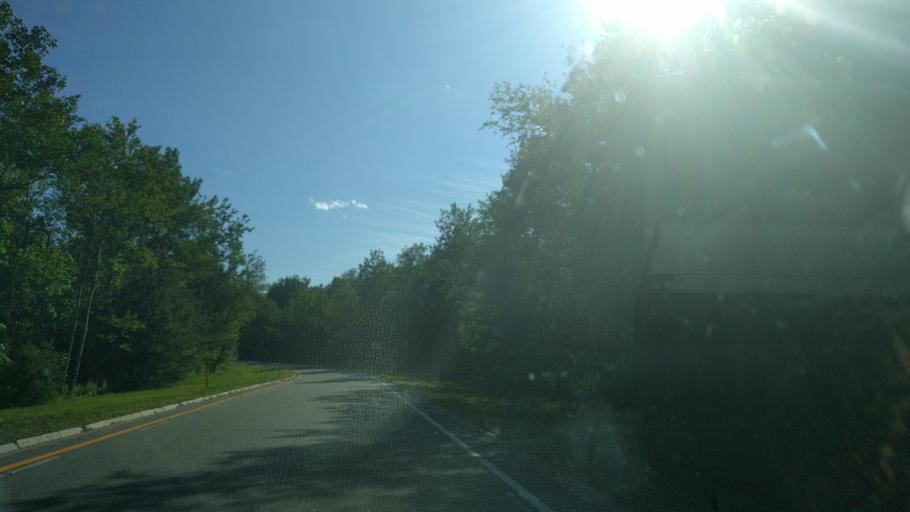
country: US
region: Massachusetts
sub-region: Worcester County
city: Oxford
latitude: 42.1541
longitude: -71.8566
